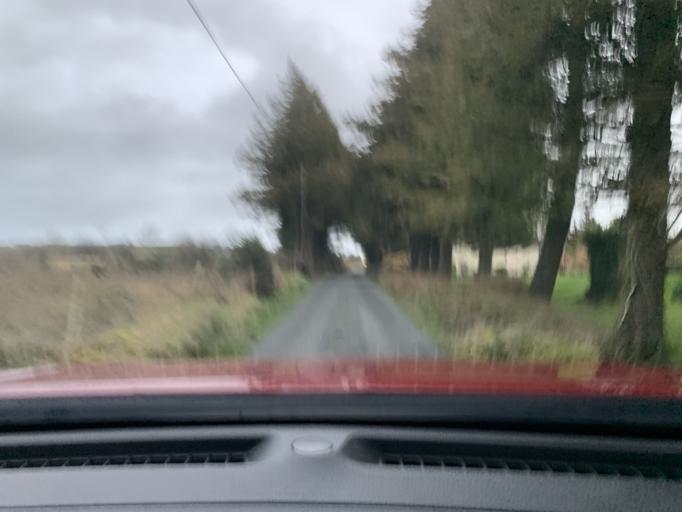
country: IE
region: Connaught
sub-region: Roscommon
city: Boyle
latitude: 53.9891
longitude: -8.3097
